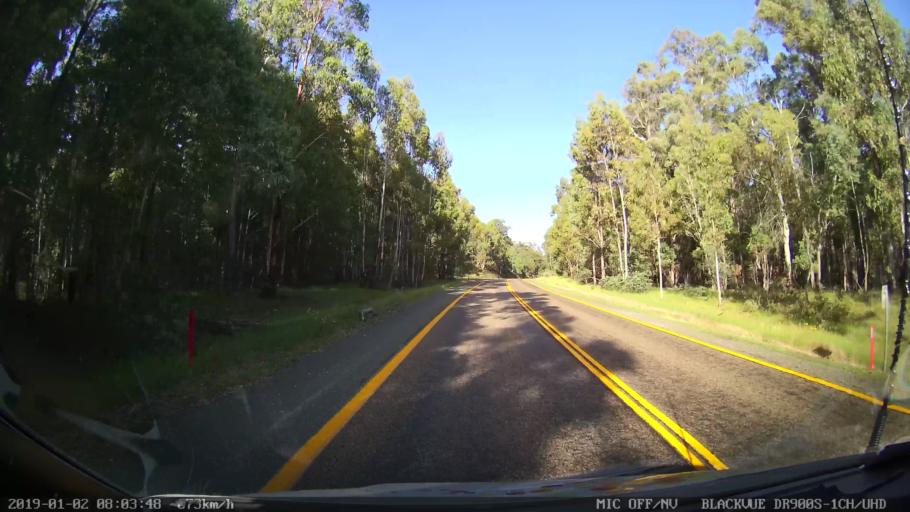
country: AU
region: New South Wales
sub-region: Tumut Shire
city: Tumut
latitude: -35.6637
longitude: 148.4032
